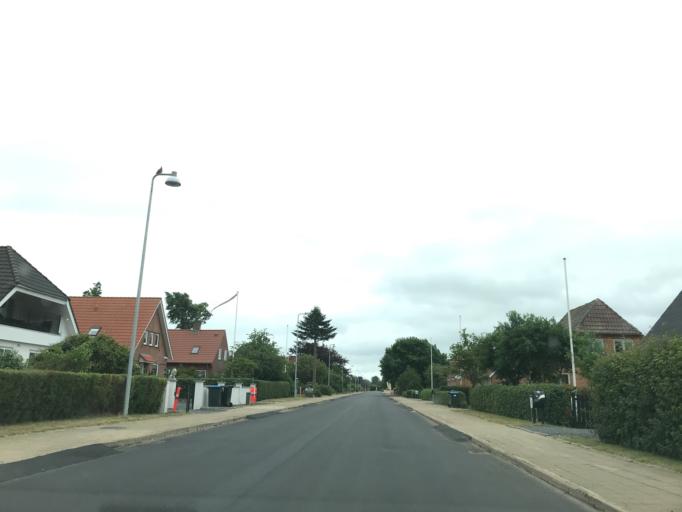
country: DK
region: South Denmark
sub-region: Tonder Kommune
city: Sherrebek
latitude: 55.0563
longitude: 8.8284
